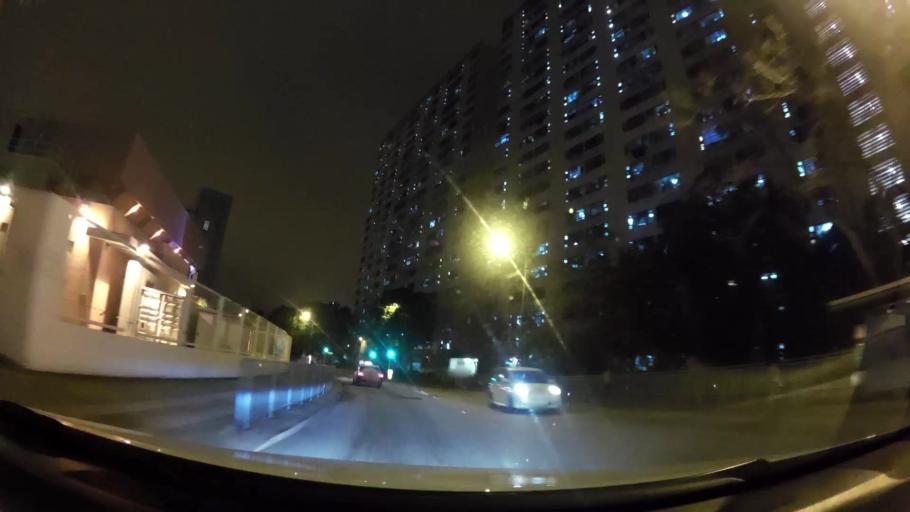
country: HK
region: Tsuen Wan
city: Tsuen Wan
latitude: 22.3466
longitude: 114.1266
